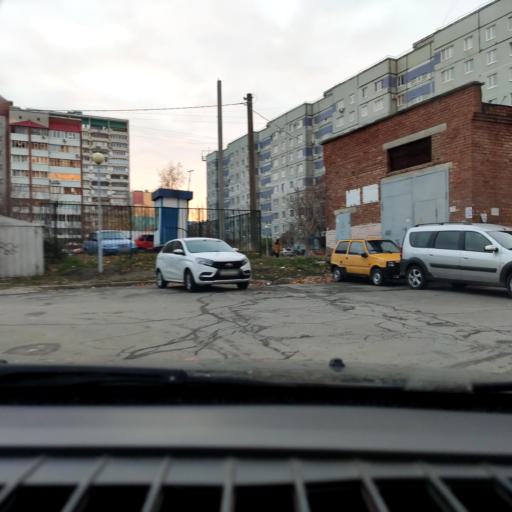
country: RU
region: Samara
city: Tol'yatti
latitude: 53.5396
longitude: 49.3363
